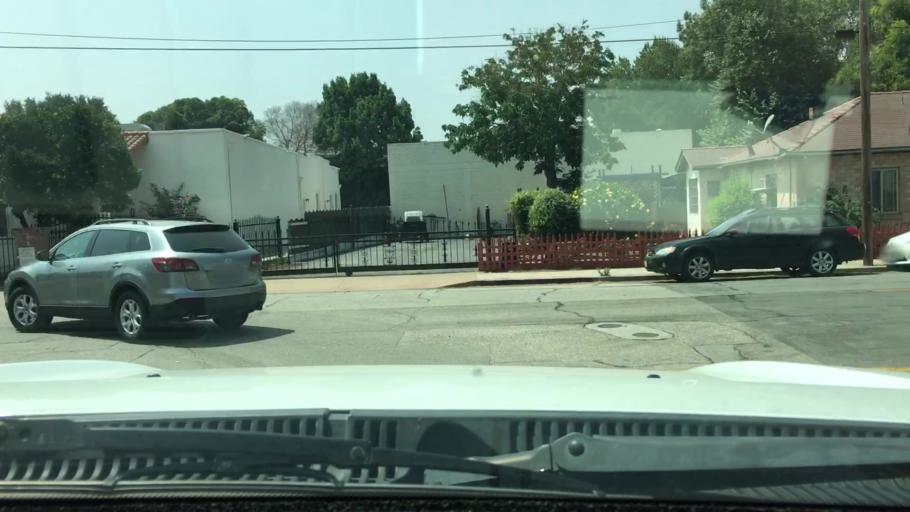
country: US
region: California
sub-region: San Luis Obispo County
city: San Luis Obispo
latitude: 35.2798
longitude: -120.6670
